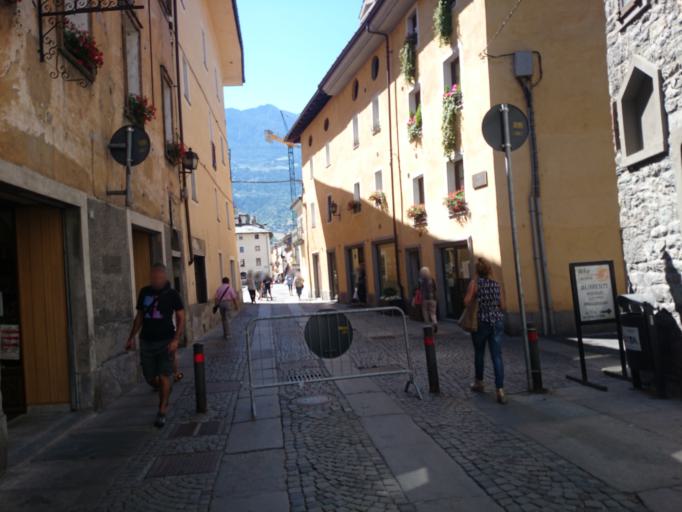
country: IT
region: Aosta Valley
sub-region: Valle d'Aosta
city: Aosta
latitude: 45.7391
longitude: 7.3155
